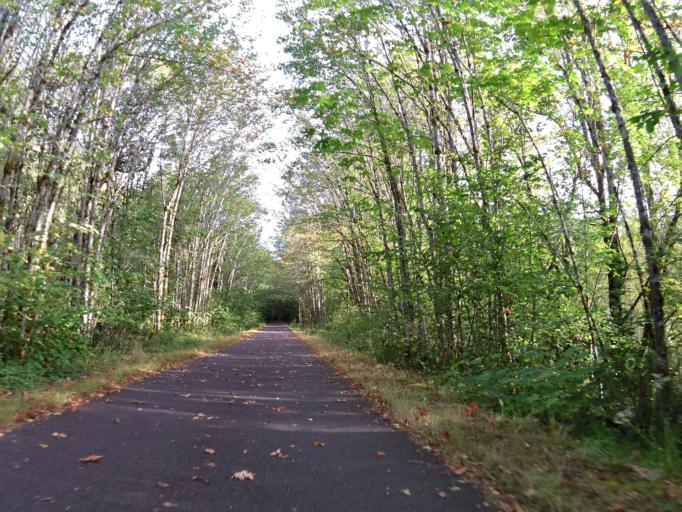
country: US
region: Washington
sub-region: Thurston County
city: Tenino
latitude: 46.9315
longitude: -122.8231
